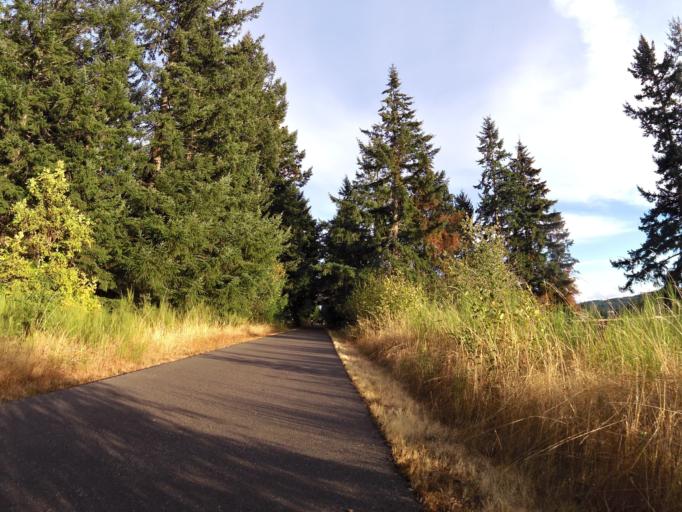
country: US
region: Washington
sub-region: Thurston County
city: Rainier
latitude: 46.8818
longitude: -122.7378
